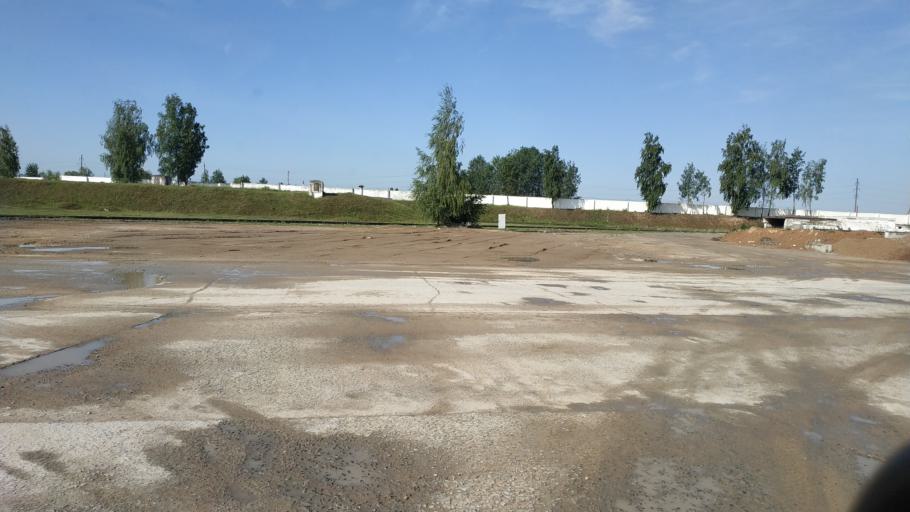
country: BY
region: Mogilev
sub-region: Mahilyowski Rayon
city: Veyno
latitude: 53.8398
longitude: 30.3837
